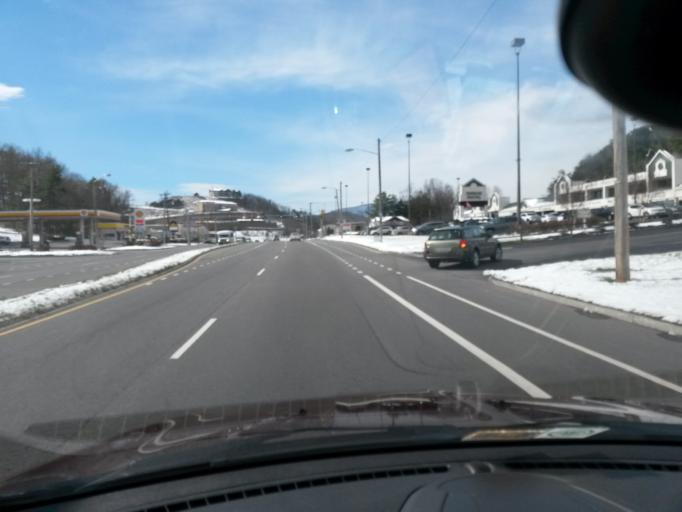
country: US
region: Virginia
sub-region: Roanoke County
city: Narrows
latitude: 37.2356
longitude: -79.9701
